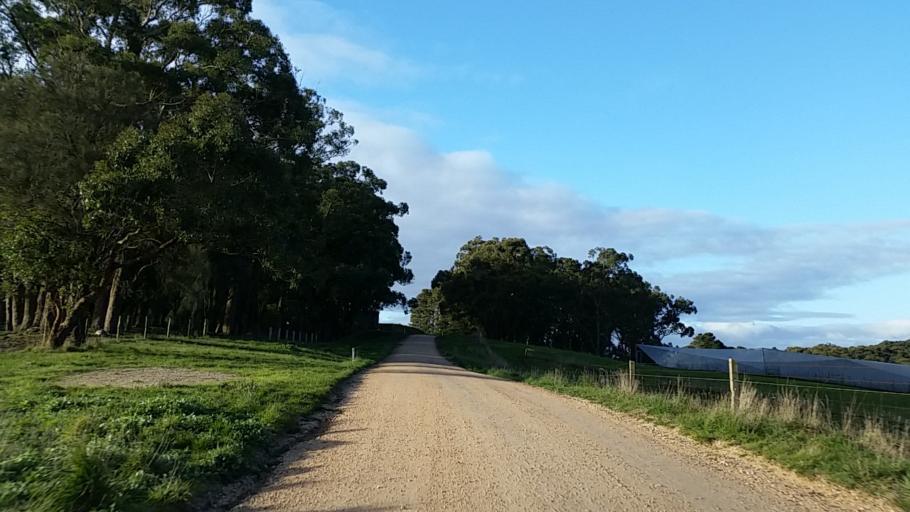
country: AU
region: South Australia
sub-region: Adelaide Hills
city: Balhannah
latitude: -34.9284
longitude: 138.7958
